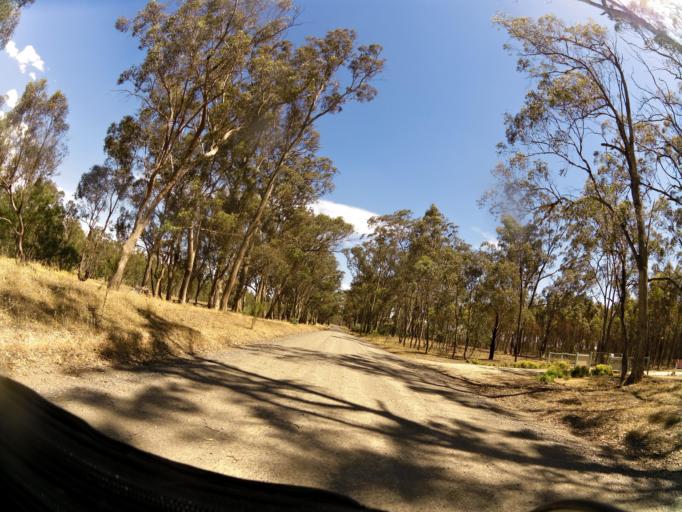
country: AU
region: Victoria
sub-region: Campaspe
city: Kyabram
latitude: -36.8251
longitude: 145.0784
